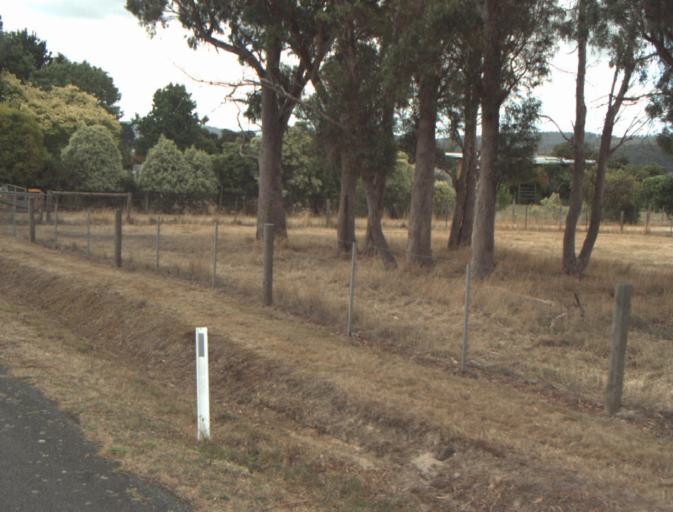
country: AU
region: Tasmania
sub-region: Launceston
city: Mayfield
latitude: -41.2891
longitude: 147.0018
